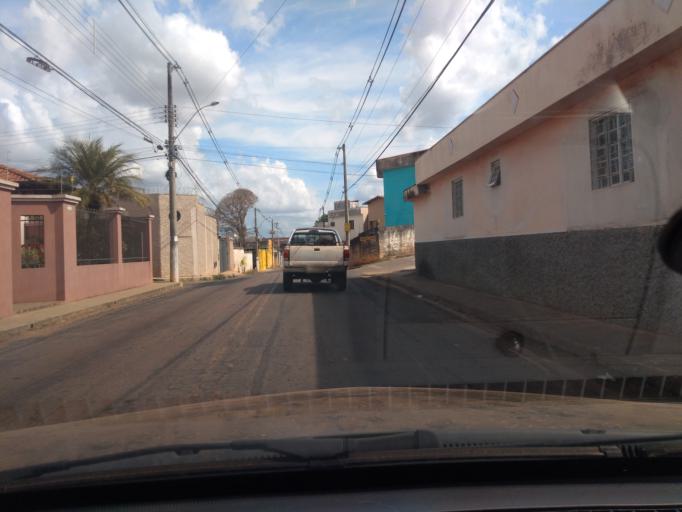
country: BR
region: Minas Gerais
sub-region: Tres Coracoes
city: Tres Coracoes
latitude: -21.7051
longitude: -45.2503
